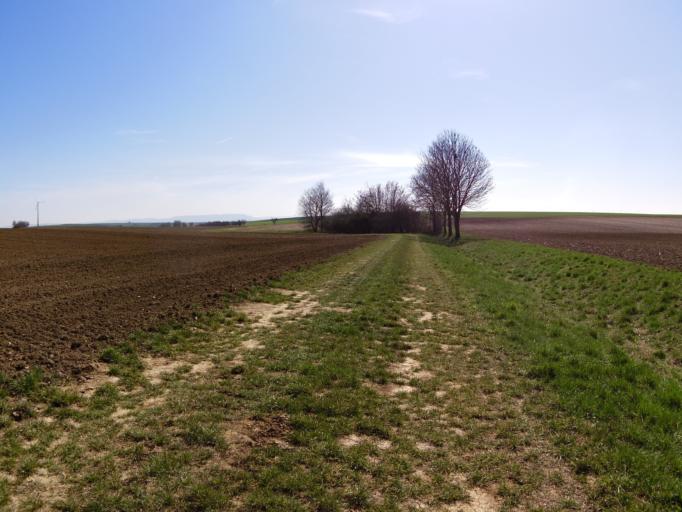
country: DE
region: Bavaria
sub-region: Regierungsbezirk Unterfranken
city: Prosselsheim
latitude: 49.8436
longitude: 10.1265
